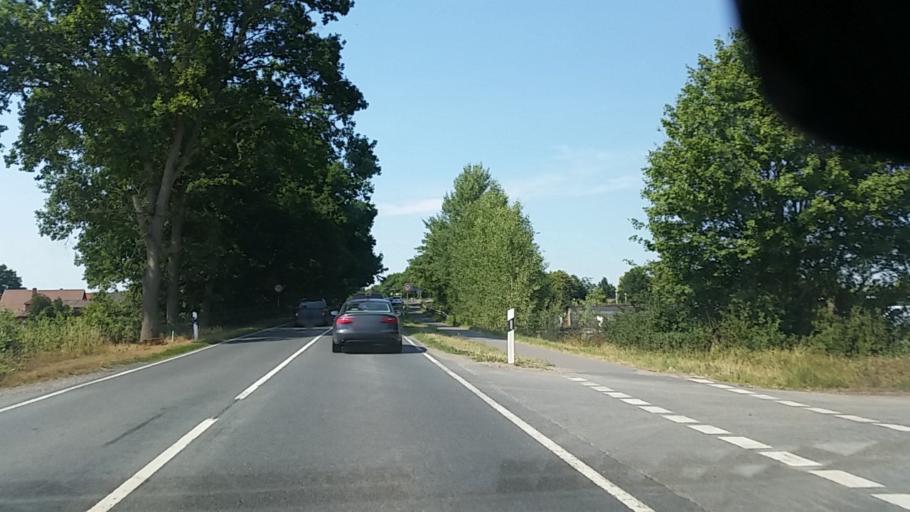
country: DE
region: Lower Saxony
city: Ottersberg
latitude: 53.0785
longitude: 9.1598
